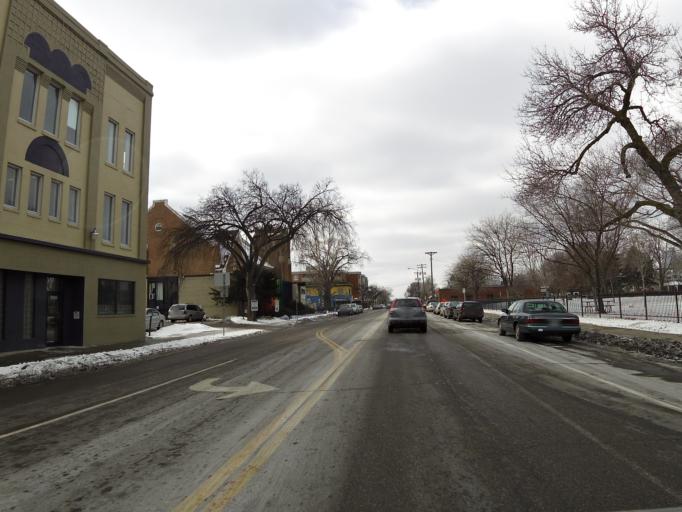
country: US
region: Minnesota
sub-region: Hennepin County
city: Minneapolis
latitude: 44.9628
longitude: -93.2347
